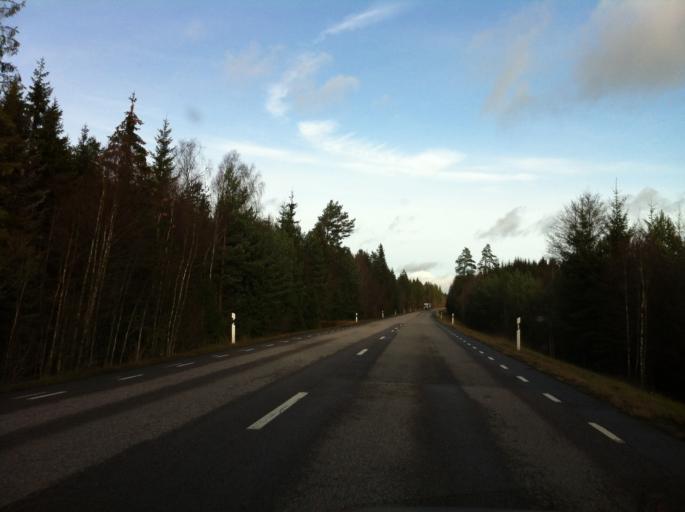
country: SE
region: Kronoberg
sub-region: Almhults Kommun
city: AElmhult
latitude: 56.6023
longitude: 14.2184
